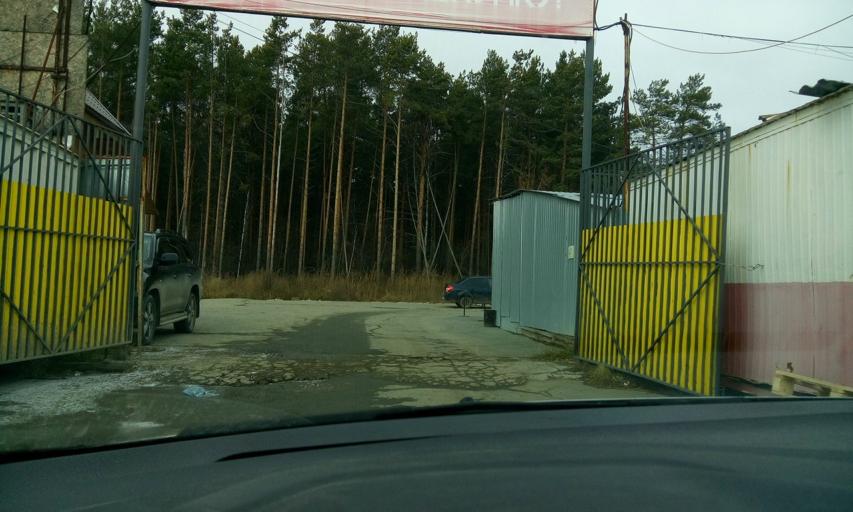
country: RU
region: Sverdlovsk
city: Sovkhoznyy
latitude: 56.7706
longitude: 60.5424
